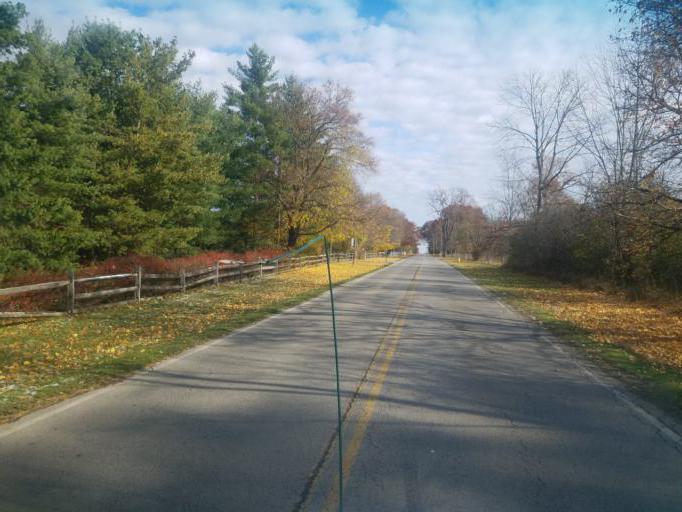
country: US
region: Ohio
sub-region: Richland County
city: Mansfield
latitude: 40.7413
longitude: -82.5467
